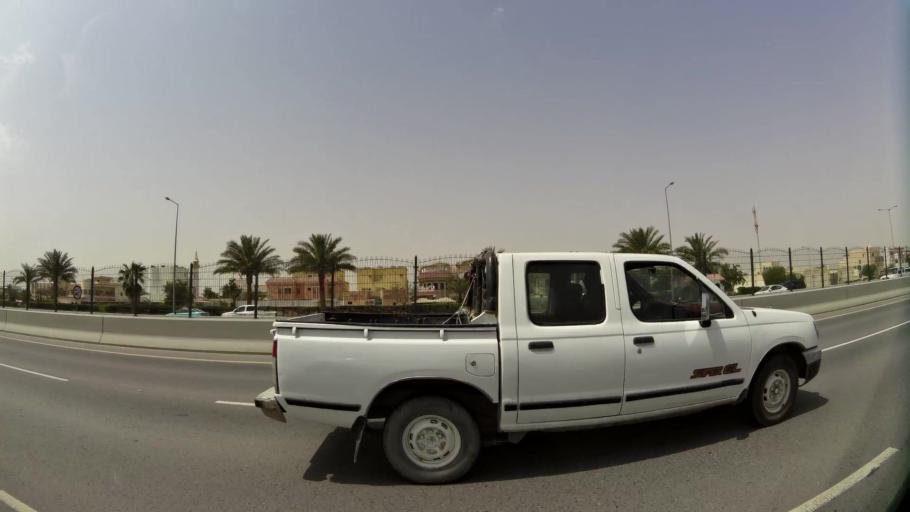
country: QA
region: Baladiyat ar Rayyan
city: Ar Rayyan
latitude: 25.2341
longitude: 51.4314
